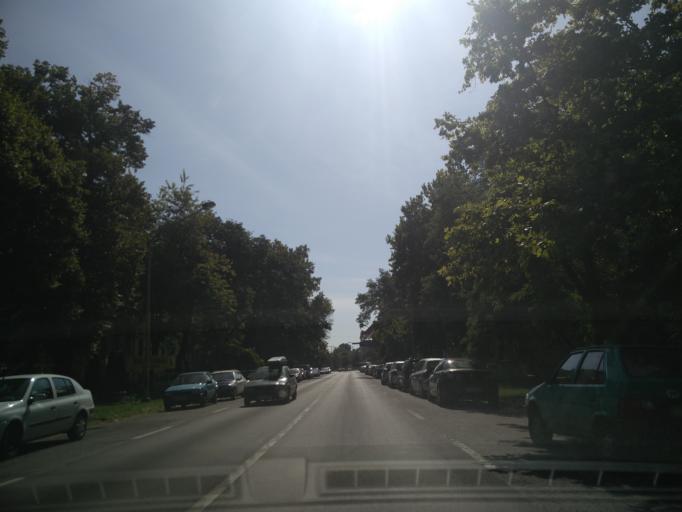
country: HU
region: Csongrad
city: Szeged
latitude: 46.2442
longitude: 20.1413
